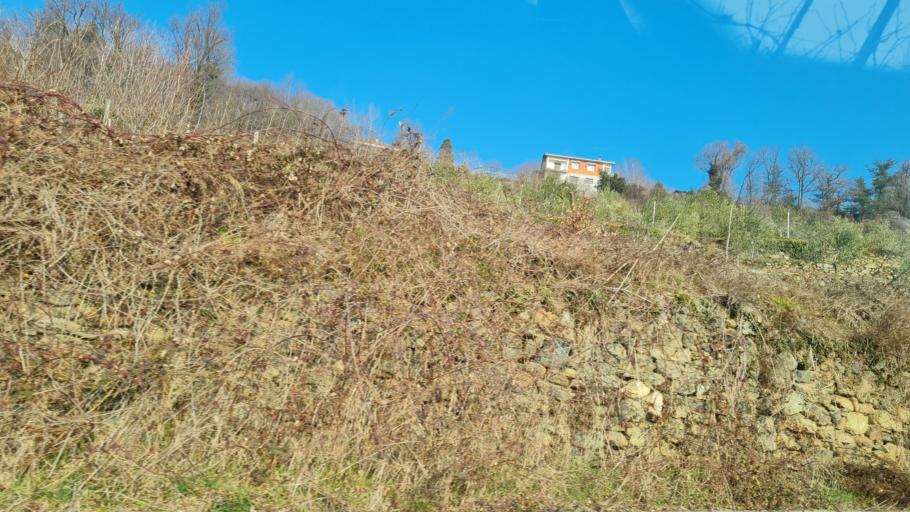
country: IT
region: Piedmont
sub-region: Provincia di Biella
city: Zimone
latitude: 45.4465
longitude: 8.0325
